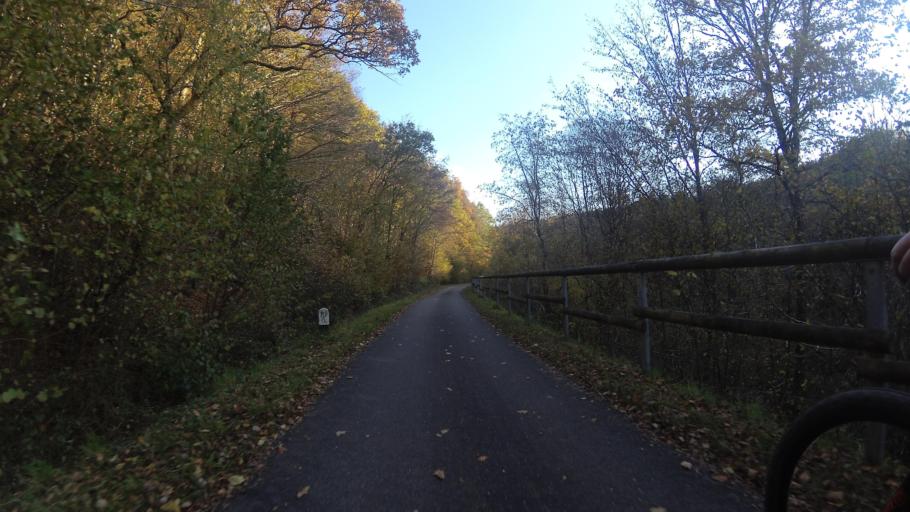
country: DE
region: Rheinland-Pfalz
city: Ollmuth
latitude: 49.6574
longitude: 6.7192
